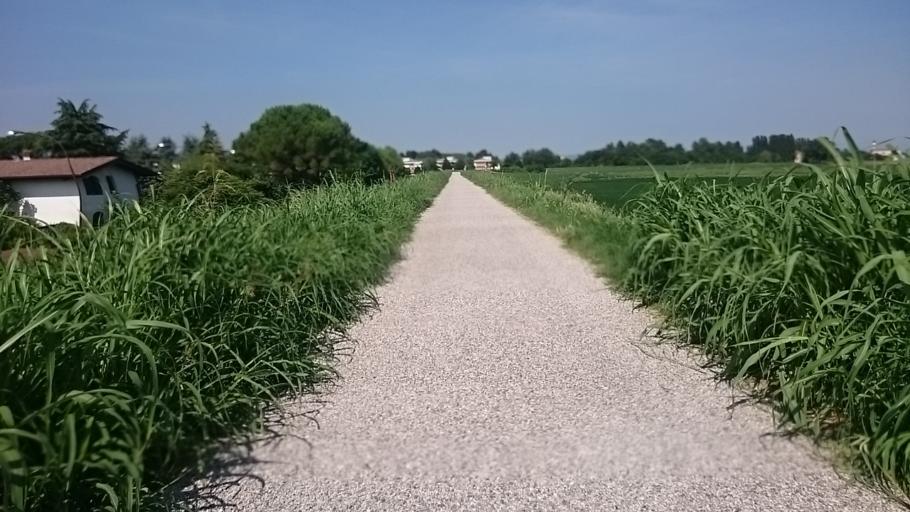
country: IT
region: Veneto
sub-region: Provincia di Padova
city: Selvazzano Dentro
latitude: 45.3915
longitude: 11.7932
